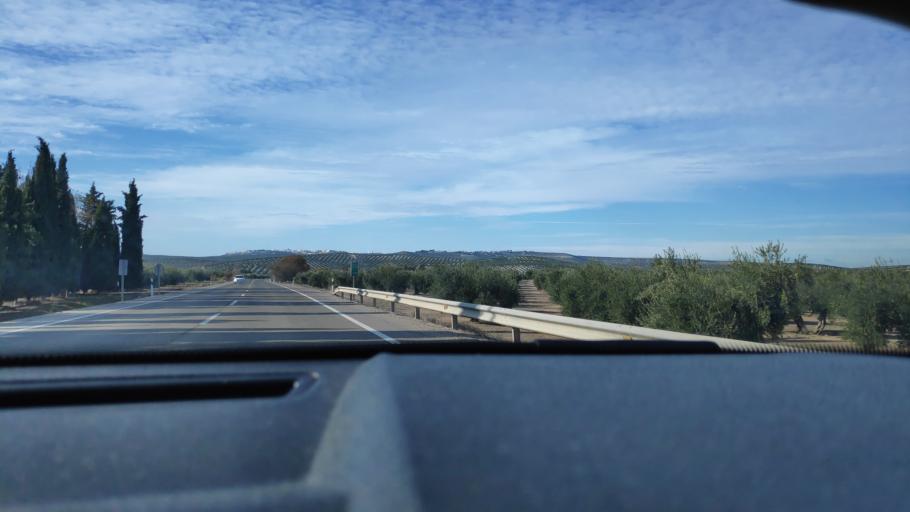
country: ES
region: Andalusia
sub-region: Provincia de Jaen
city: Higuera de Calatrava
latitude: 37.8462
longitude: -4.1211
